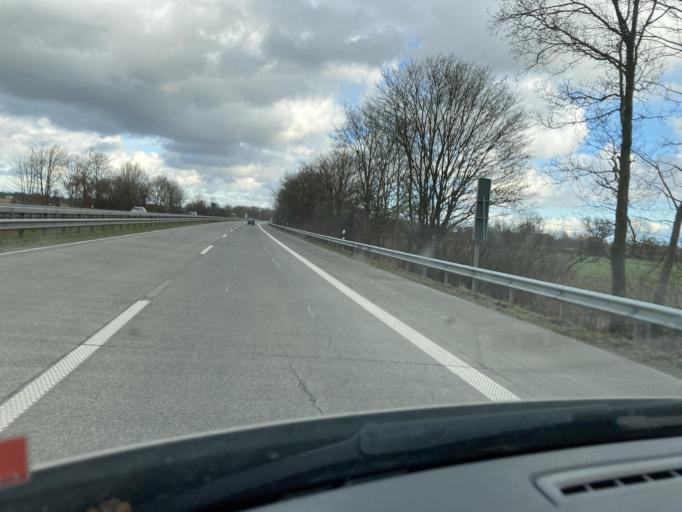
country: DE
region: Lower Saxony
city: Fedderwarden
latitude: 53.5544
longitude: 8.0657
